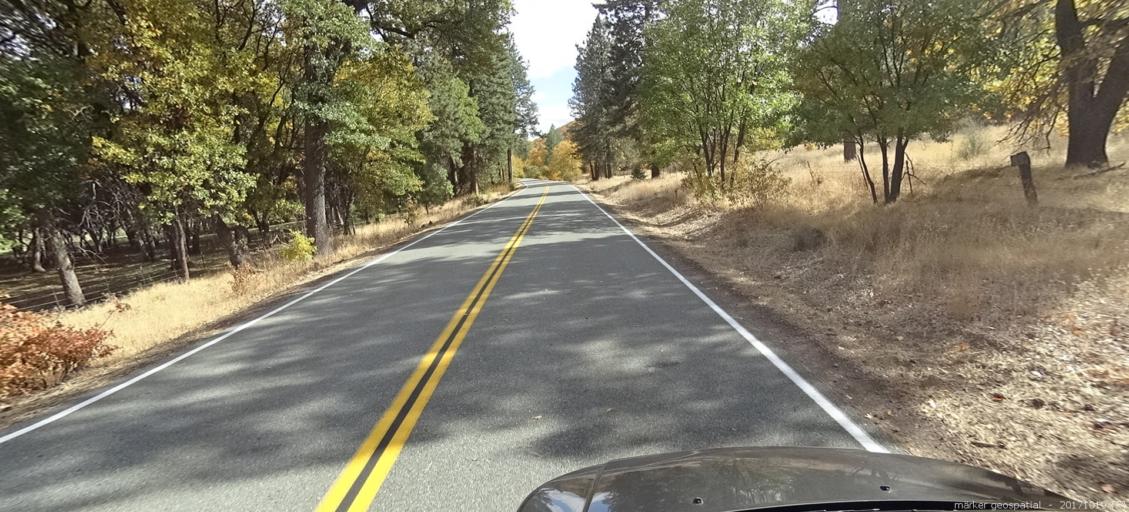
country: US
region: California
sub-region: Shasta County
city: Burney
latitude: 41.0302
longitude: -121.4831
